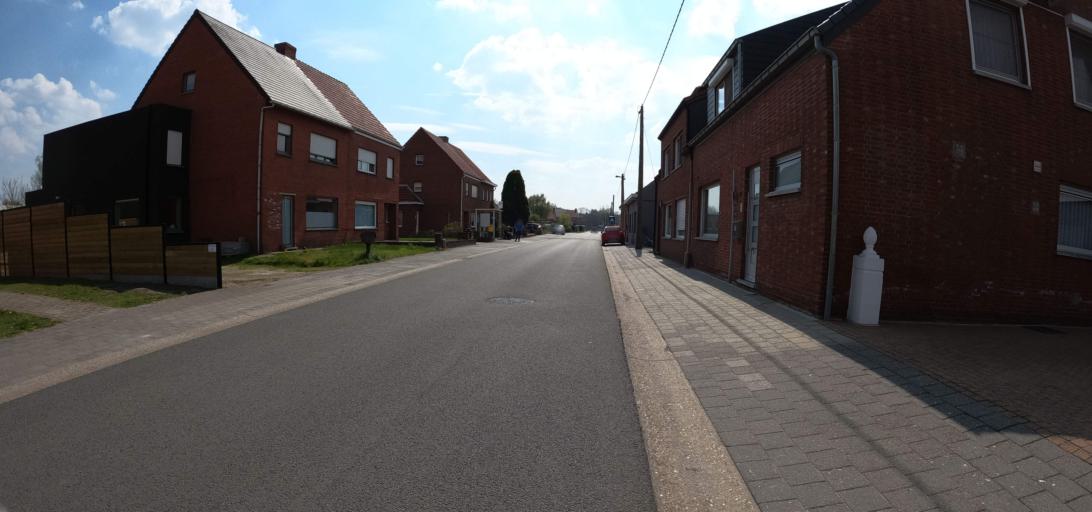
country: BE
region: Flanders
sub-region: Provincie Antwerpen
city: Rijkevorsel
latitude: 51.3293
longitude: 4.7884
